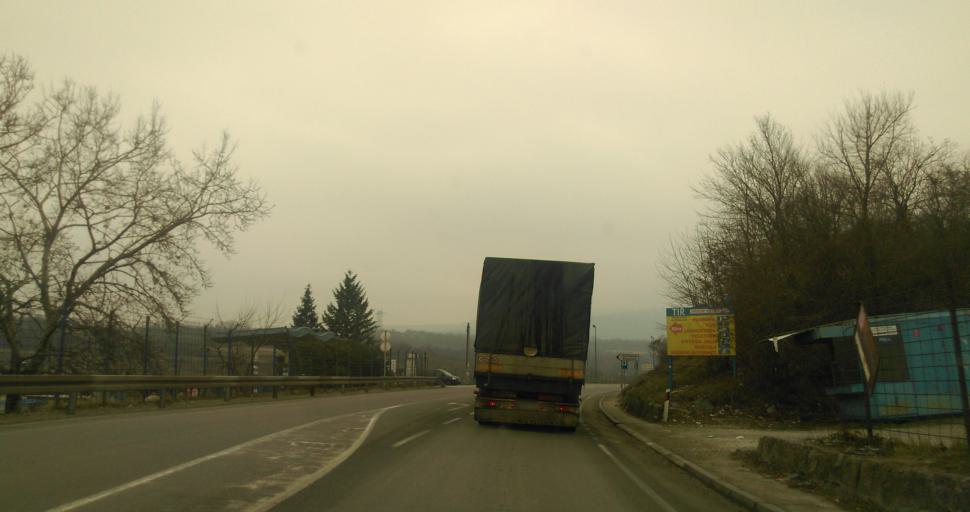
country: RS
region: Central Serbia
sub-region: Belgrade
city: Zvezdara
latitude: 44.7206
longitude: 20.5408
